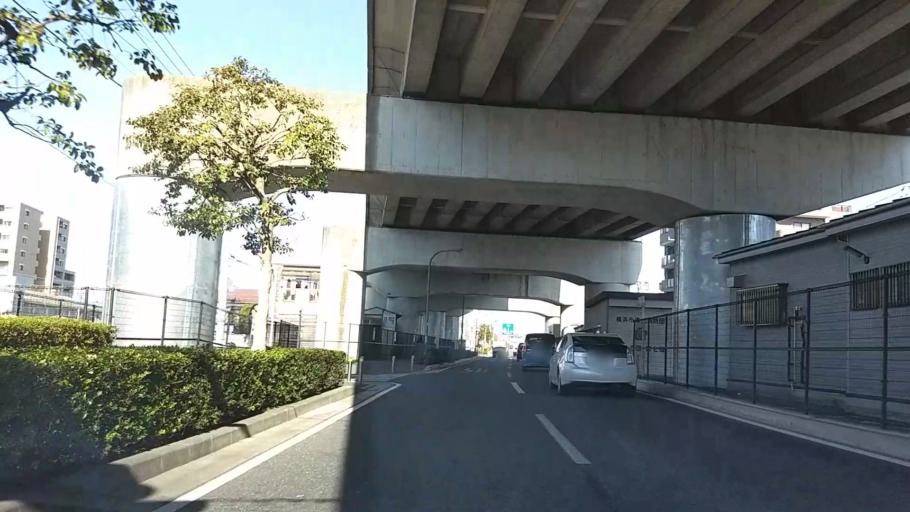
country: JP
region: Kanagawa
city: Yokohama
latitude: 35.5250
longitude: 139.6122
